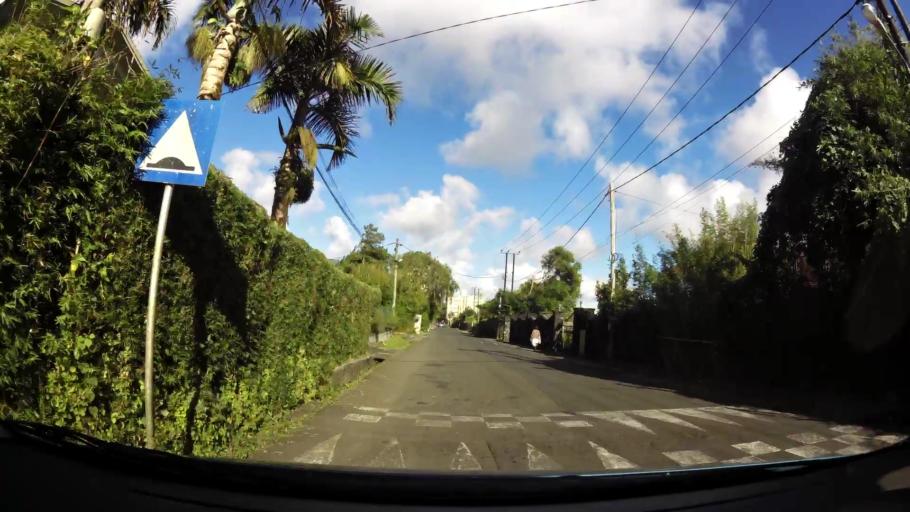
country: MU
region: Plaines Wilhems
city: Curepipe
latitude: -20.3173
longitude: 57.5323
